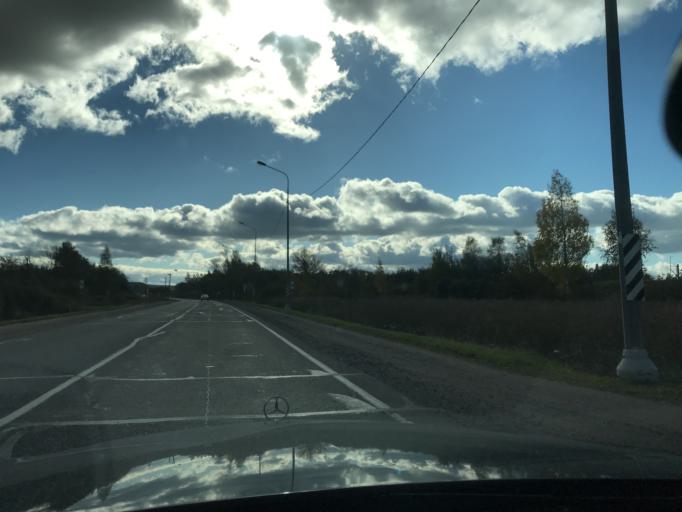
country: RU
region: Pskov
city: Ostrov
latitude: 57.3223
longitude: 28.3643
